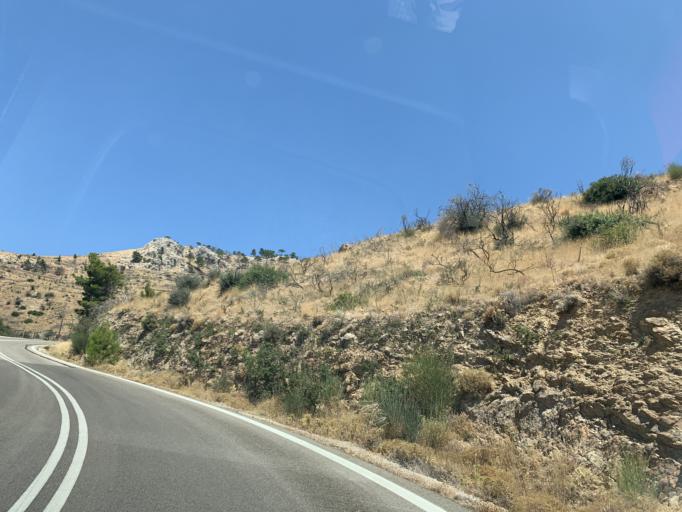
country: GR
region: North Aegean
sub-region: Chios
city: Vrontados
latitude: 38.4524
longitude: 25.9776
